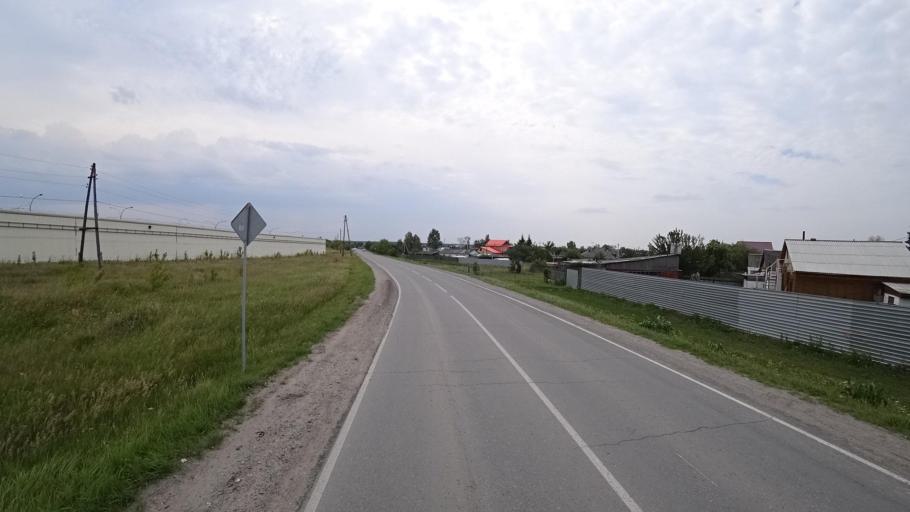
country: RU
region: Sverdlovsk
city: Kamyshlov
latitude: 56.8555
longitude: 62.7350
